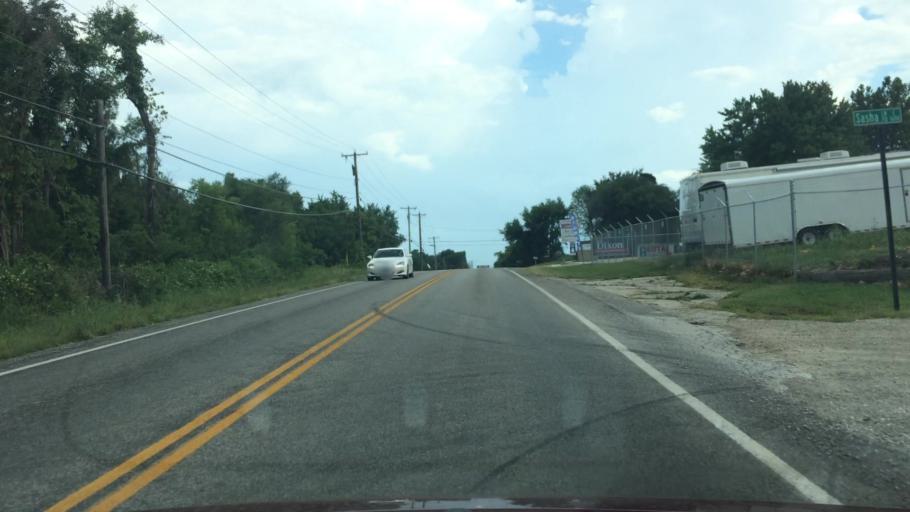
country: US
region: Missouri
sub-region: Greene County
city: Springfield
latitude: 37.2710
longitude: -93.2646
